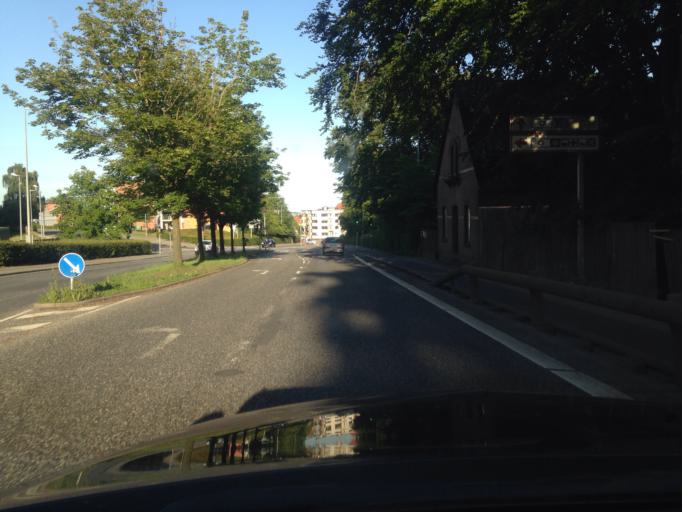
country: DK
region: South Denmark
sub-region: Kolding Kommune
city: Kolding
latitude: 55.4951
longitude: 9.4596
